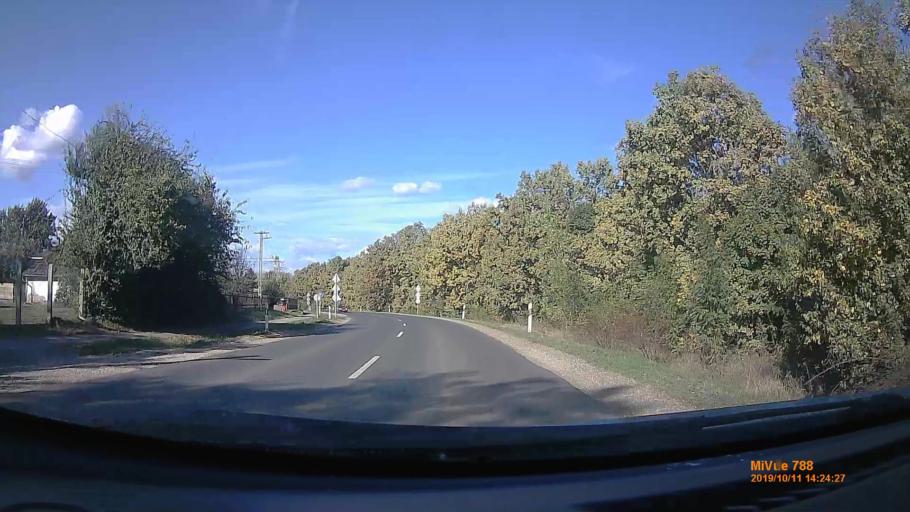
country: HU
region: Hajdu-Bihar
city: Balmazujvaros
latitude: 47.5342
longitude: 21.3571
